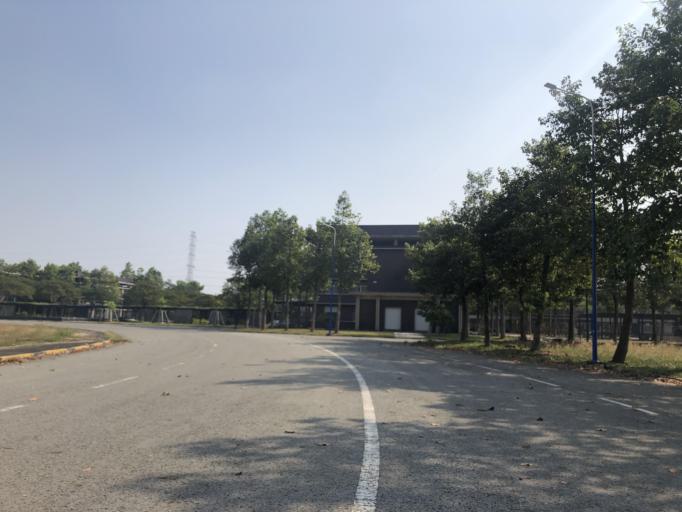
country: VN
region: Binh Duong
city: Thu Dau Mot
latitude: 11.0522
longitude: 106.6662
